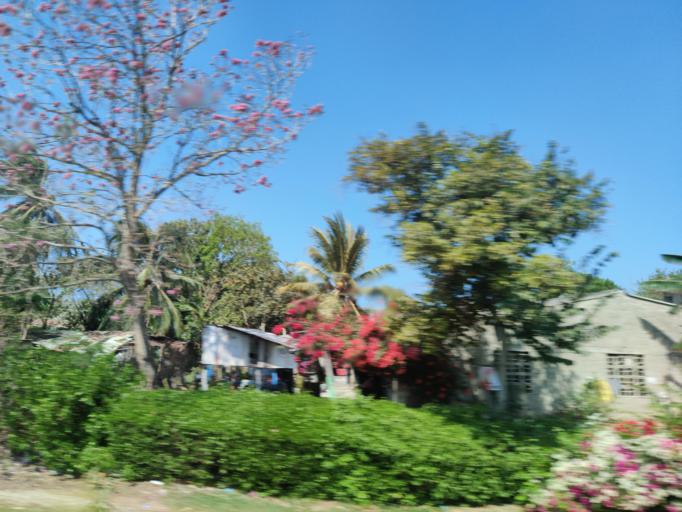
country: CO
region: Bolivar
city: Santa Catalina
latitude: 10.7370
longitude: -75.2617
